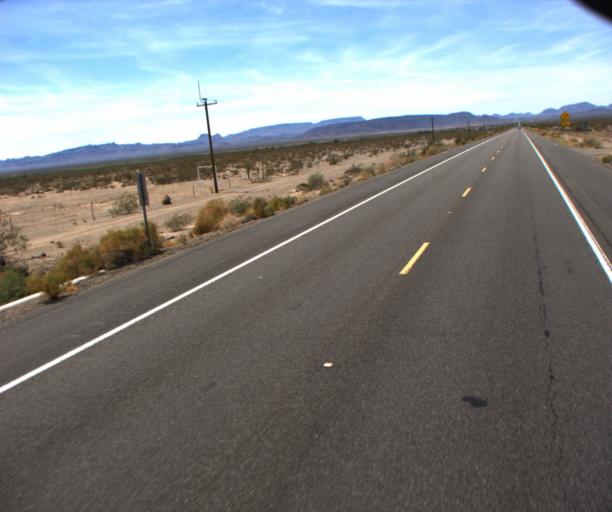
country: US
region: Arizona
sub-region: La Paz County
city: Salome
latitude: 33.7166
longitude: -113.7810
